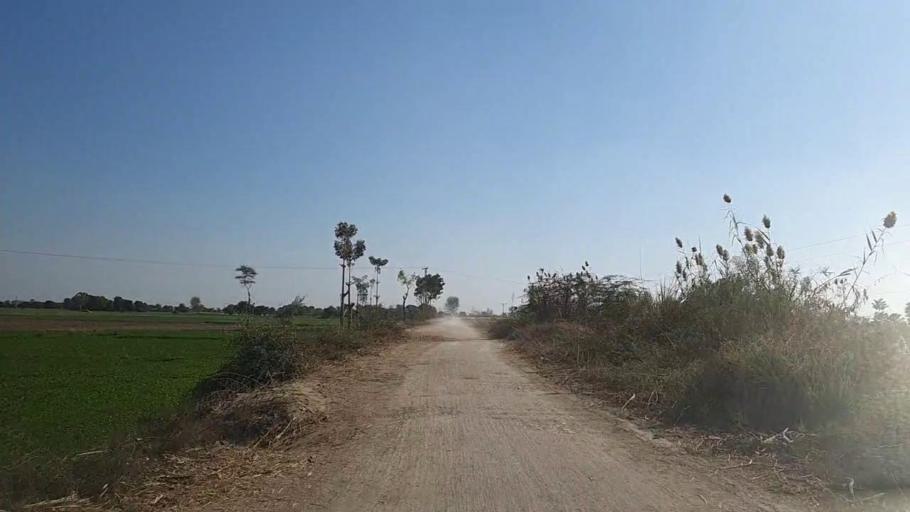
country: PK
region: Sindh
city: Nawabshah
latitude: 26.2261
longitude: 68.4287
